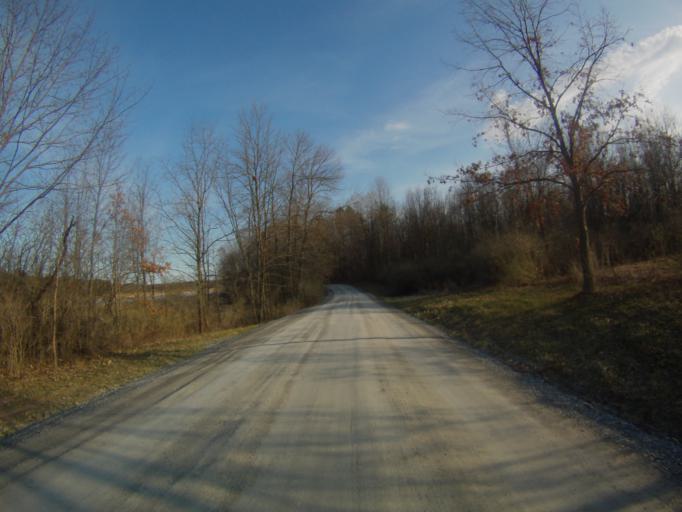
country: US
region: New York
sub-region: Essex County
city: Port Henry
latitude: 44.0782
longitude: -73.3507
